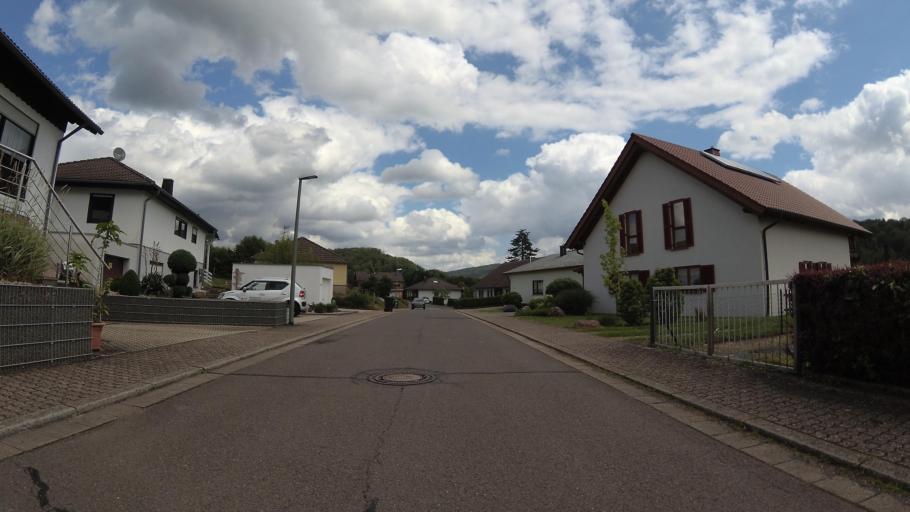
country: DE
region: Saarland
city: Nonnweiler
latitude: 49.6101
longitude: 6.9688
